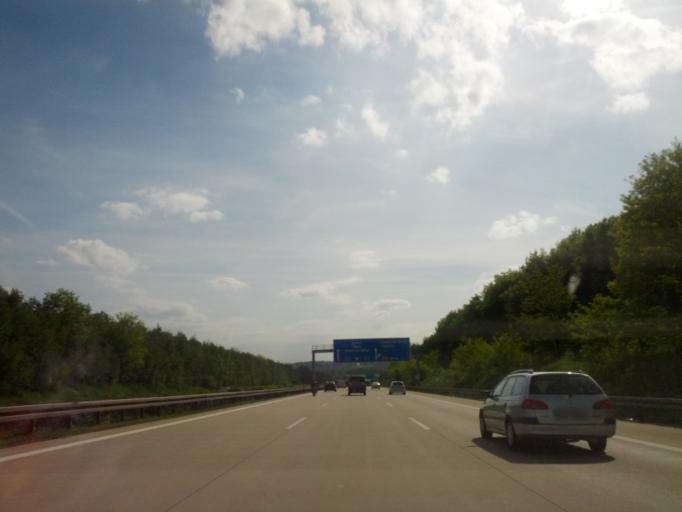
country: DE
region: Saxony
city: Chemnitz
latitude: 50.8815
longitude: 12.9238
